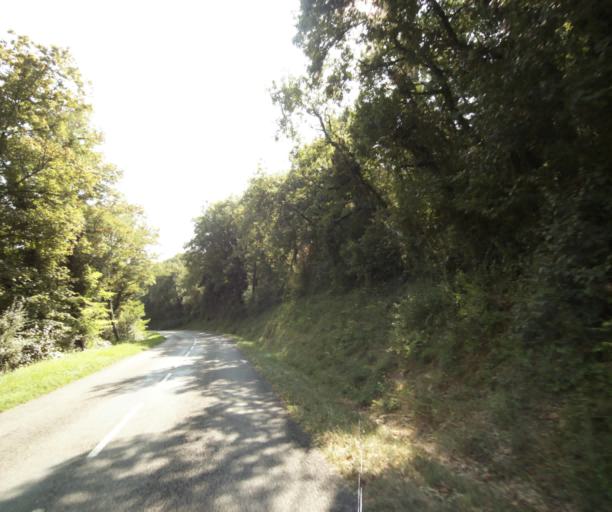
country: FR
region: Bourgogne
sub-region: Departement de Saone-et-Loire
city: Tournus
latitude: 46.5570
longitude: 4.8764
